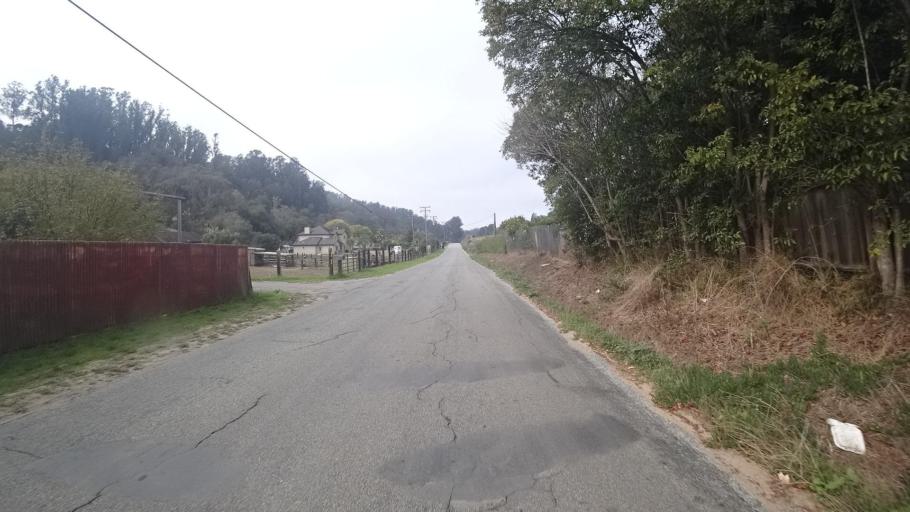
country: US
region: California
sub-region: Monterey County
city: Las Lomas
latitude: 36.8829
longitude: -121.7154
